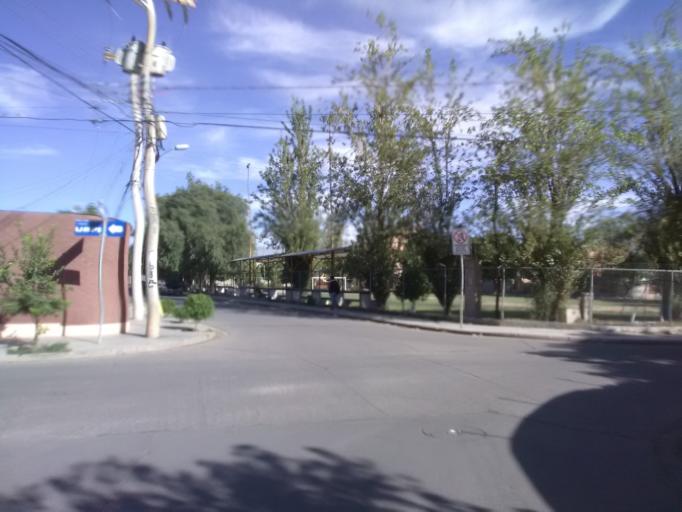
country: BO
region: Cochabamba
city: Cochabamba
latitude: -17.3745
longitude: -66.1891
